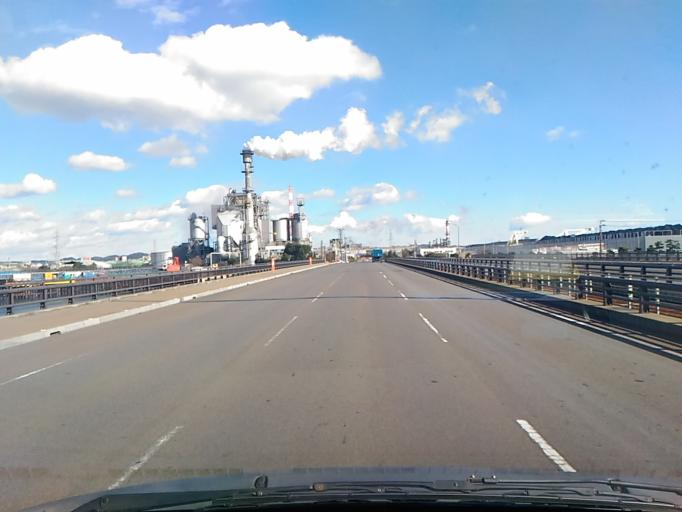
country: JP
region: Fukushima
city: Iwaki
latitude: 36.9352
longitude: 140.8709
